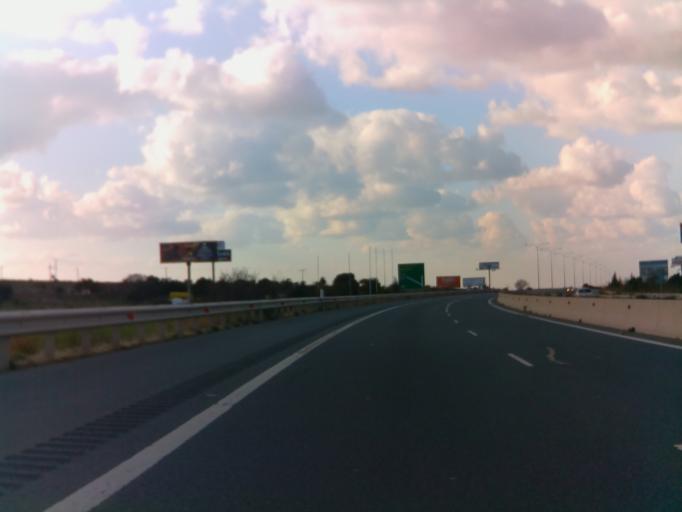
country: CY
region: Pafos
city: Paphos
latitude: 34.7704
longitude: 32.4669
